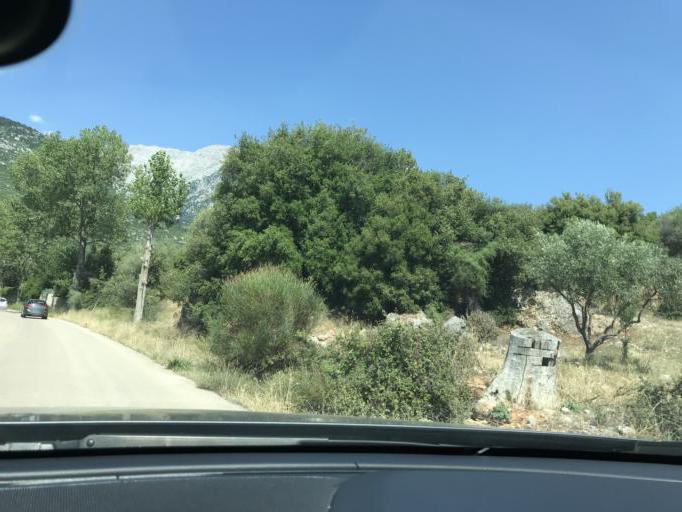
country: GR
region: Central Greece
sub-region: Nomos Voiotias
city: Distomo
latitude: 38.5109
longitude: 22.7135
